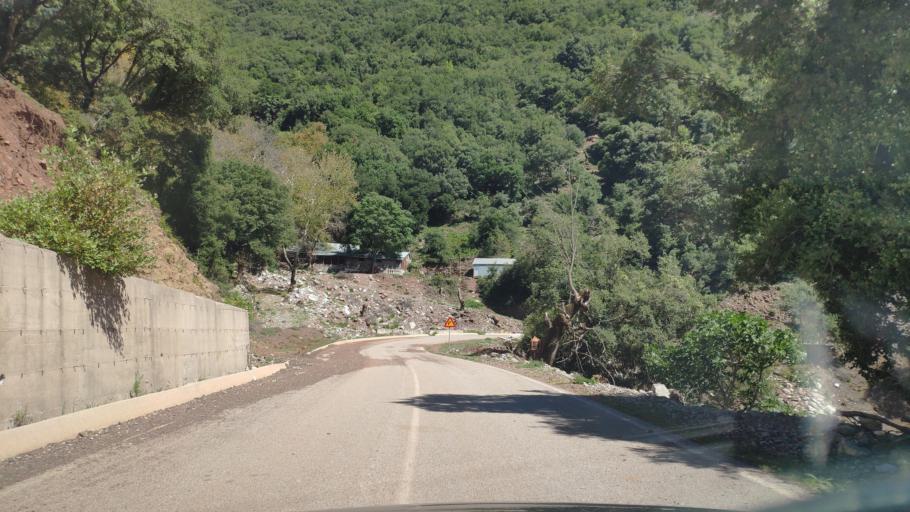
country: GR
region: Central Greece
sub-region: Nomos Evrytanias
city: Kerasochori
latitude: 39.0895
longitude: 21.5971
